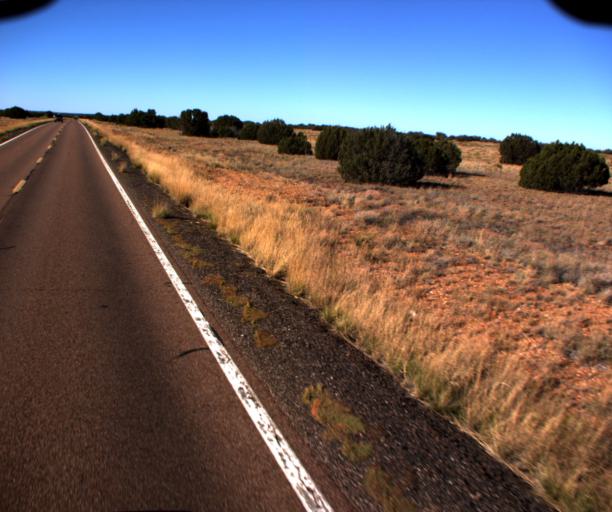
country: US
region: Arizona
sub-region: Navajo County
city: Heber-Overgaard
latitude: 34.5768
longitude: -110.4086
